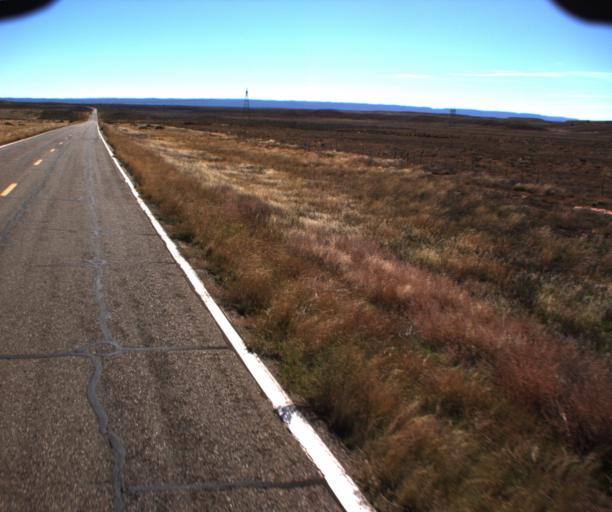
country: US
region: Arizona
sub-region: Coconino County
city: Fredonia
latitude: 36.9200
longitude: -112.4366
